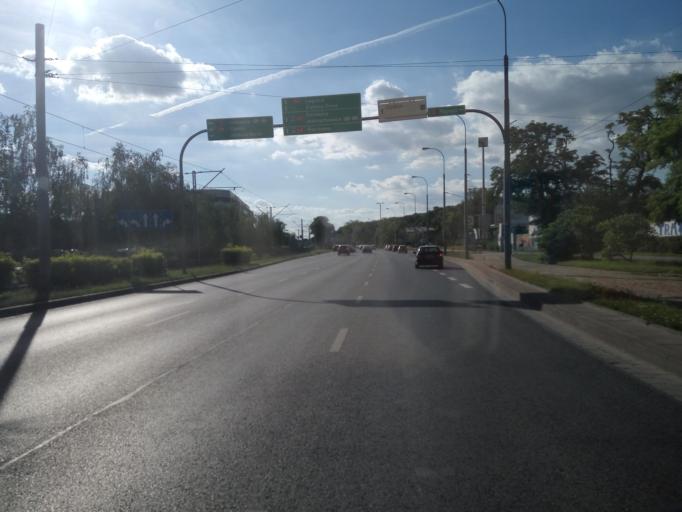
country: PL
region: Lower Silesian Voivodeship
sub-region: Powiat wroclawski
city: Wroclaw
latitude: 51.1261
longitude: 16.9822
